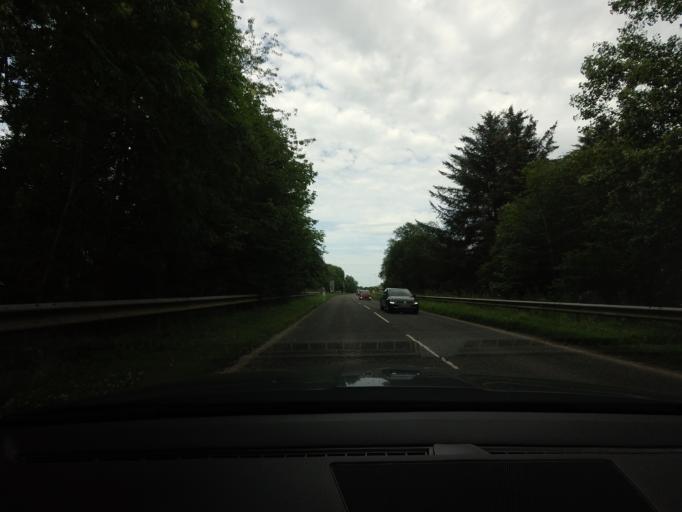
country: GB
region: Scotland
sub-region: Highland
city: Alness
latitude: 57.6912
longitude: -4.2733
